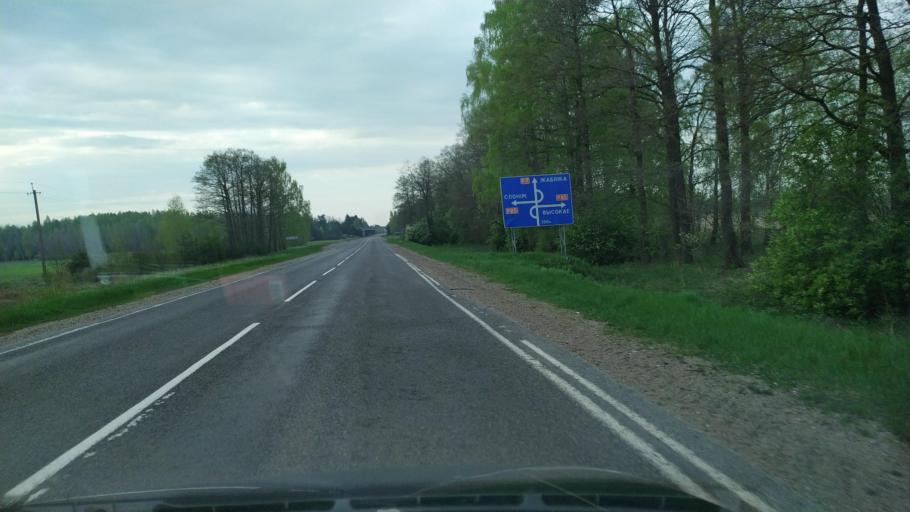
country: BY
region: Brest
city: Kamyanyets
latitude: 52.3468
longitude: 23.9028
